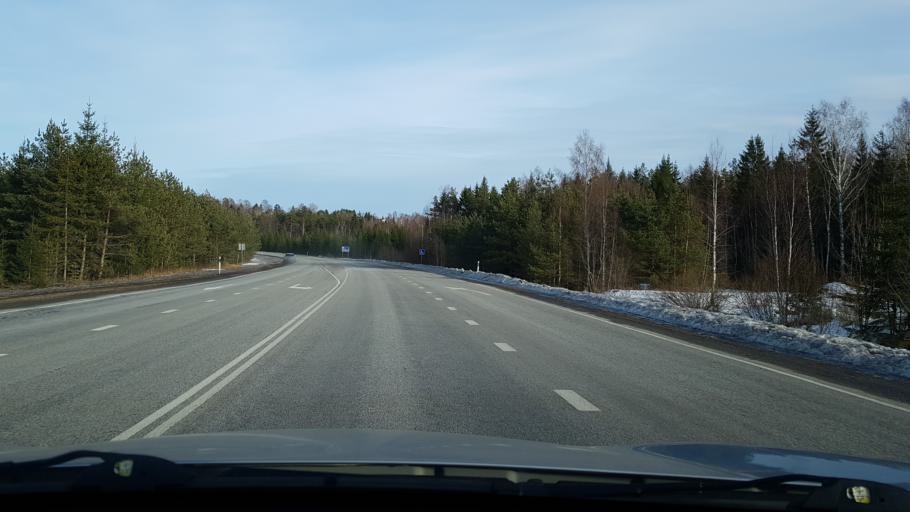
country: EE
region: Viljandimaa
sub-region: Viljandi linn
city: Viljandi
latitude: 58.3387
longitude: 25.4786
